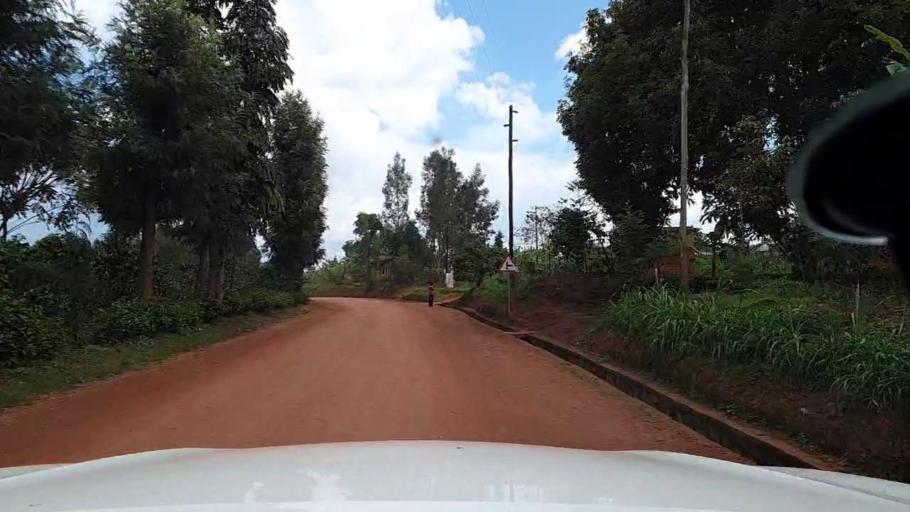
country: RW
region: Kigali
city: Kigali
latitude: -1.8086
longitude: 29.8419
